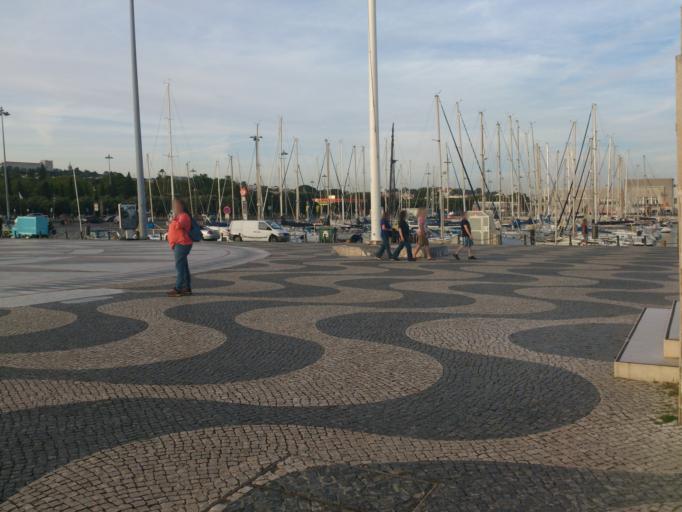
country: PT
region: Lisbon
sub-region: Oeiras
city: Alges
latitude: 38.6938
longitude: -9.2058
